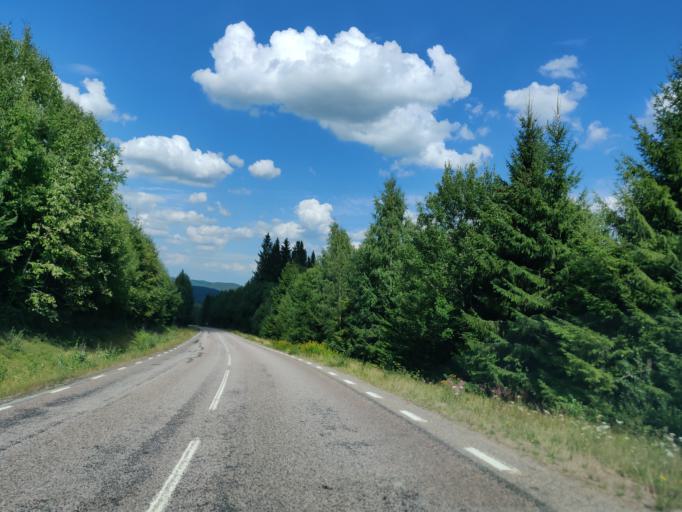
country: SE
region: Vaermland
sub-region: Munkfors Kommun
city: Munkfors
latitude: 59.8654
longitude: 13.6941
